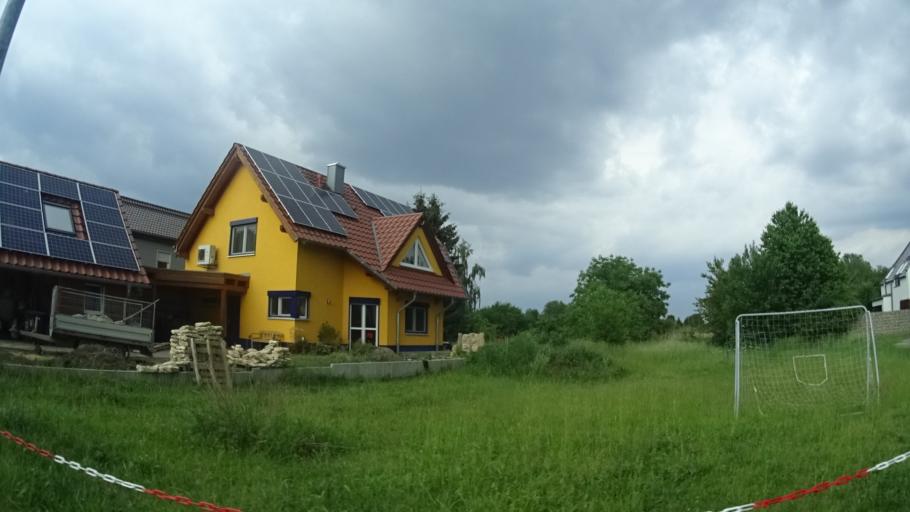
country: DE
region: Rheinland-Pfalz
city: Schifferstadt
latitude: 49.3824
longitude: 8.3629
